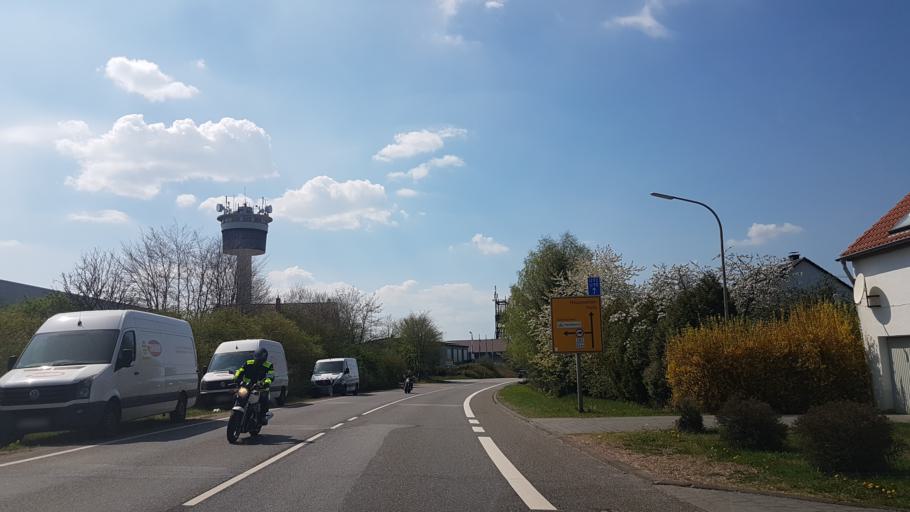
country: DE
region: Saarland
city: Merchweiler
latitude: 49.3356
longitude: 7.0078
